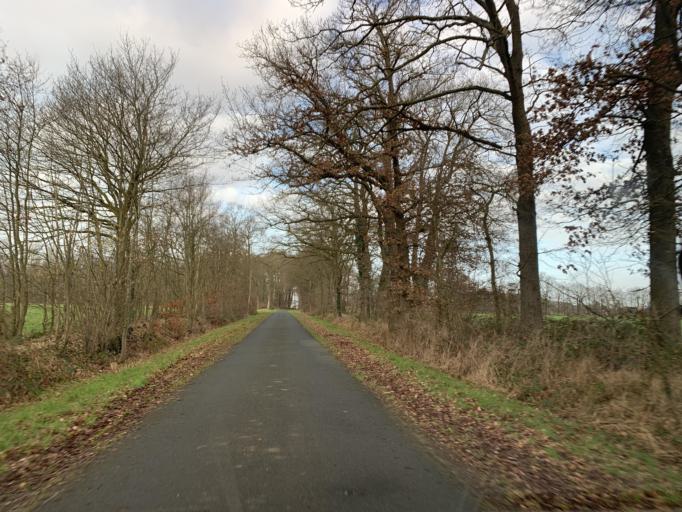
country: DE
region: North Rhine-Westphalia
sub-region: Regierungsbezirk Munster
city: Greven
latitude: 52.0479
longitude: 7.6287
